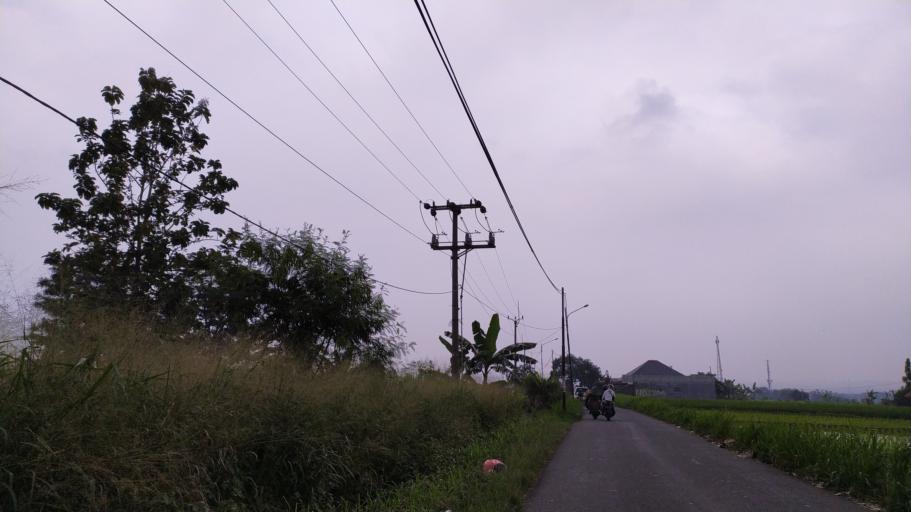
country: ID
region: West Java
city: Ciampea
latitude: -6.6105
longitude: 106.6985
